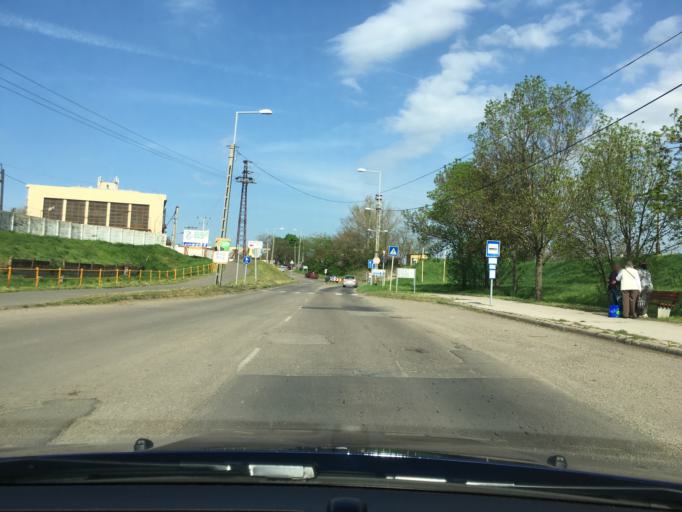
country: HU
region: Csongrad
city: Hodmezovasarhely
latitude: 46.4119
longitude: 20.3352
